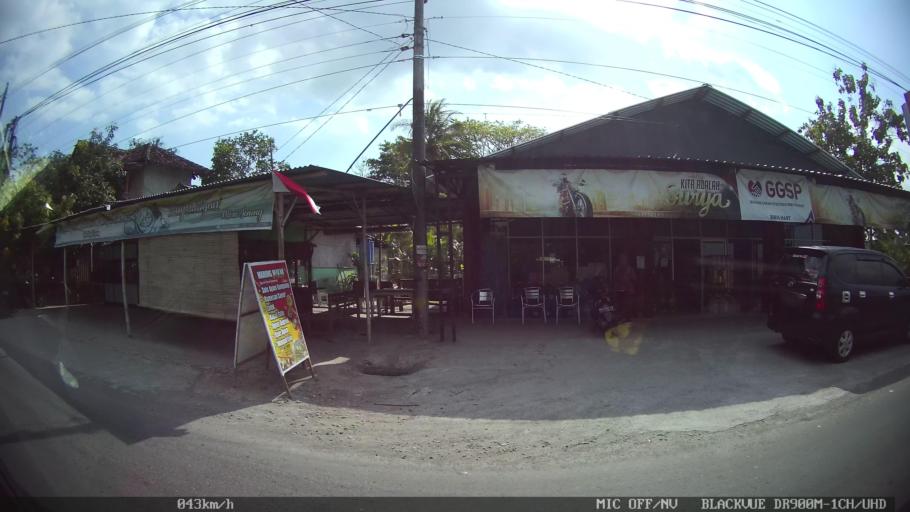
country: ID
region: Daerah Istimewa Yogyakarta
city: Kasihan
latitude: -7.8487
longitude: 110.3146
